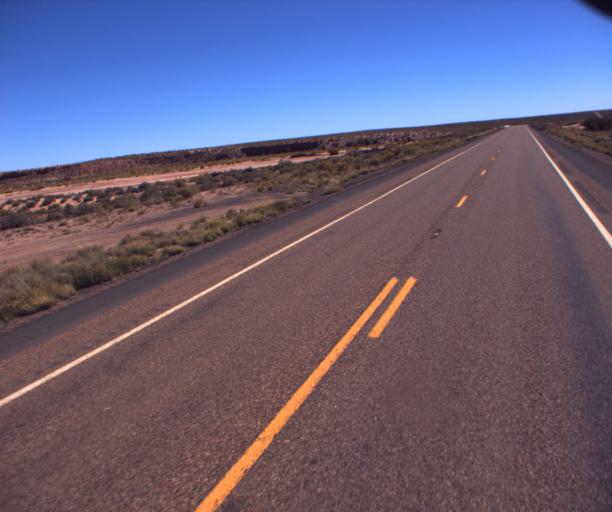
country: US
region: Arizona
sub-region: Navajo County
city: Holbrook
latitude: 35.0666
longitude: -110.0992
